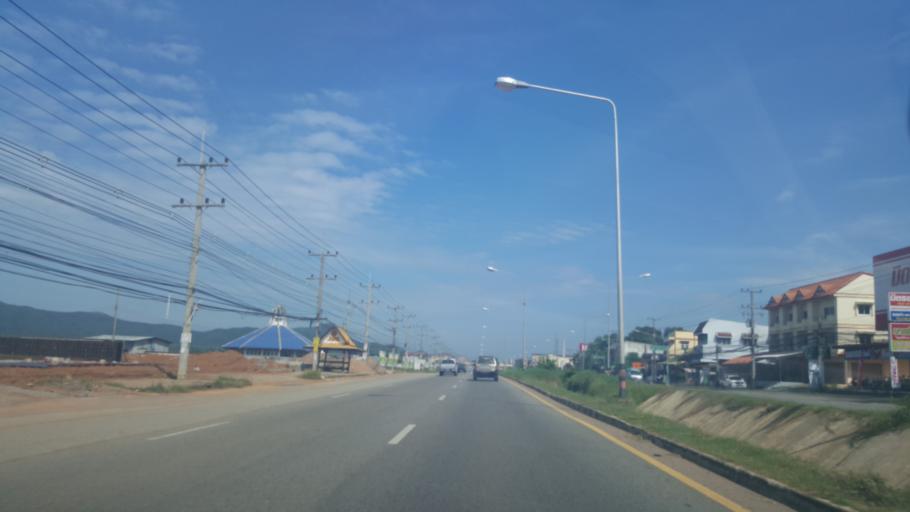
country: TH
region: Chon Buri
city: Sattahip
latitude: 12.6981
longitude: 100.8909
